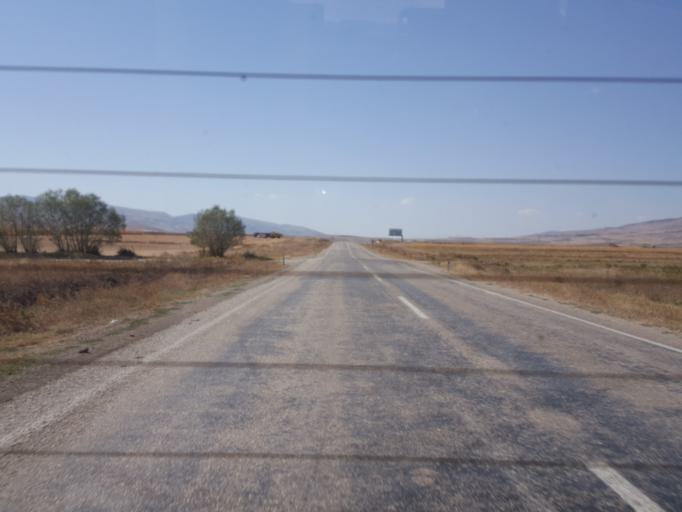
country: TR
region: Amasya
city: Dogantepe
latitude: 40.5773
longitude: 35.6185
